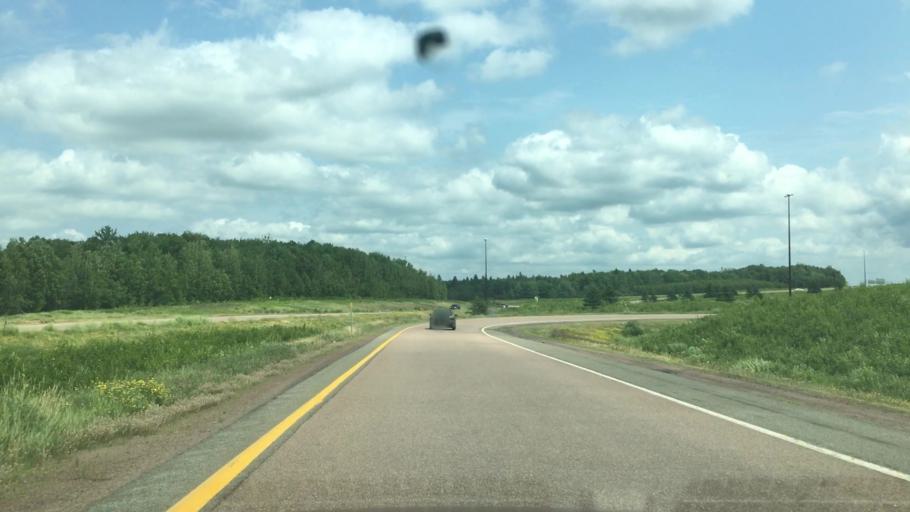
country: CA
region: New Brunswick
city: Dieppe
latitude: 46.1295
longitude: -64.6822
